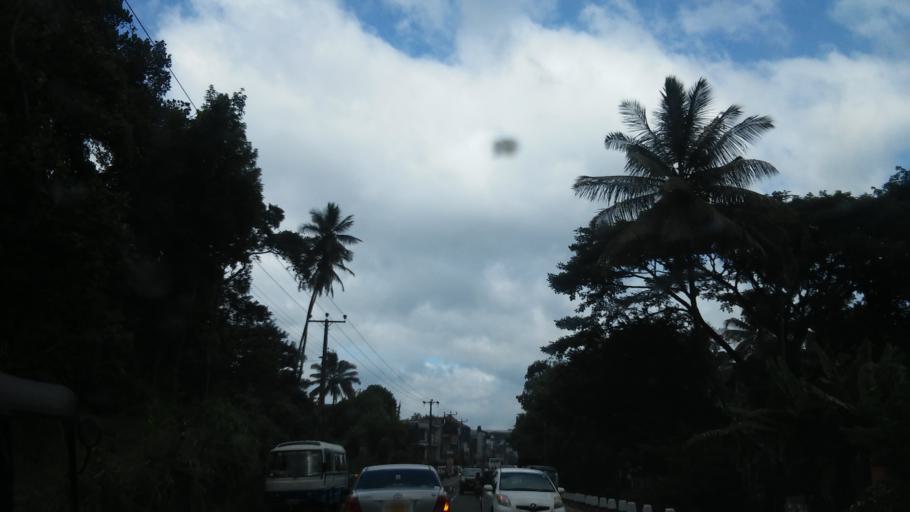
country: LK
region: Central
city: Kandy
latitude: 7.2815
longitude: 80.6228
